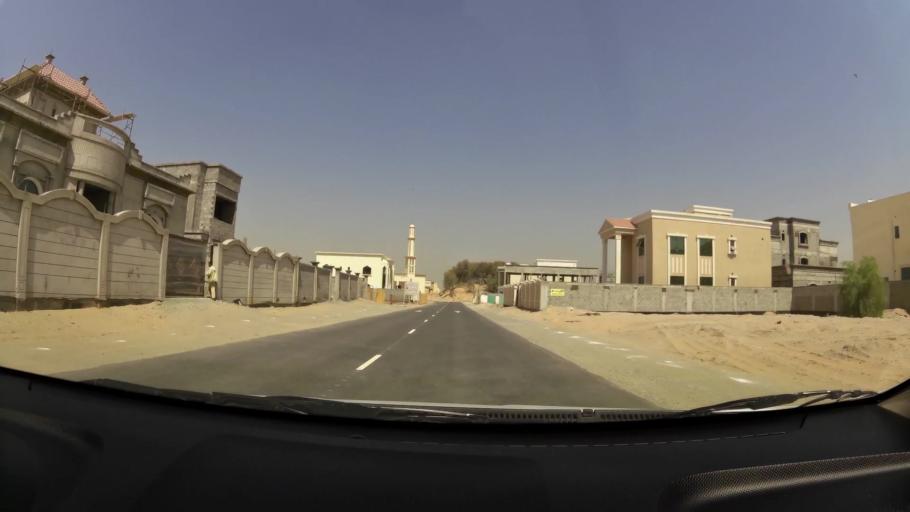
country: AE
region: Ajman
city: Ajman
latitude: 25.4054
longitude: 55.5325
